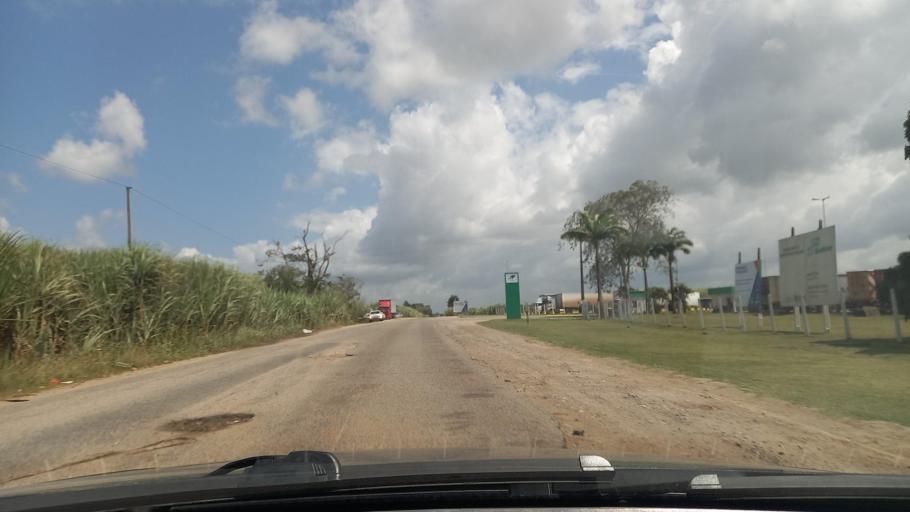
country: BR
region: Pernambuco
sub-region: Goiana
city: Goiana
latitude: -7.5579
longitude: -35.0355
